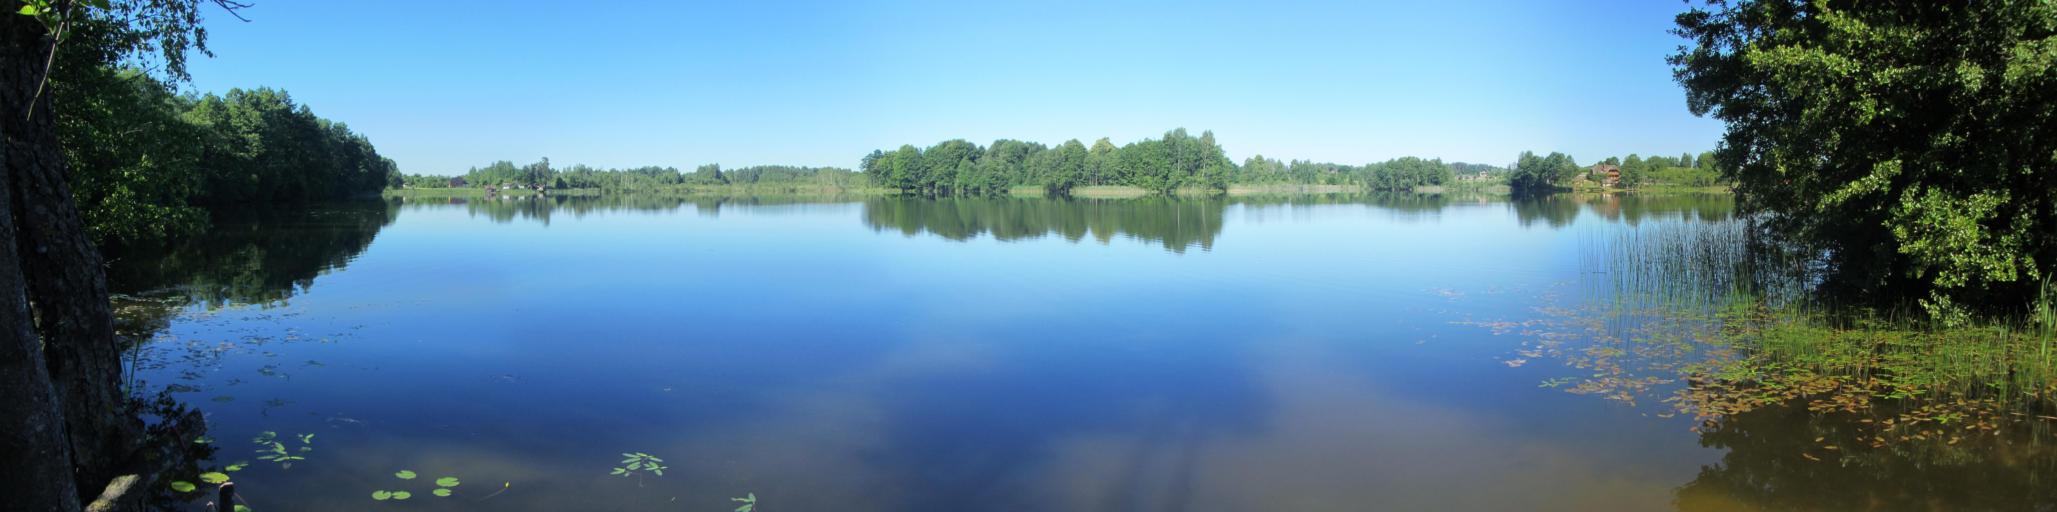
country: LT
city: Trakai
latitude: 54.6921
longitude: 24.9599
